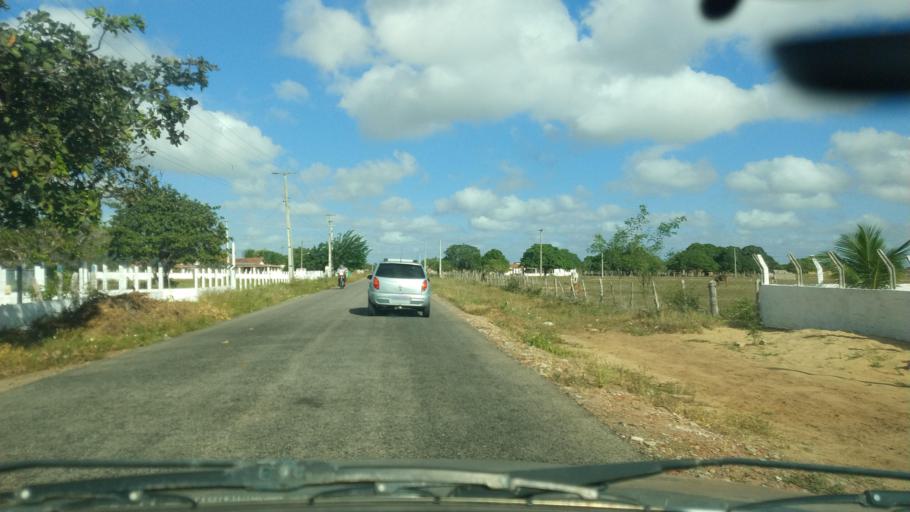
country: BR
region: Rio Grande do Norte
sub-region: Sao Paulo Do Potengi
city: Sao Paulo do Potengi
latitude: -5.9160
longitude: -35.7176
